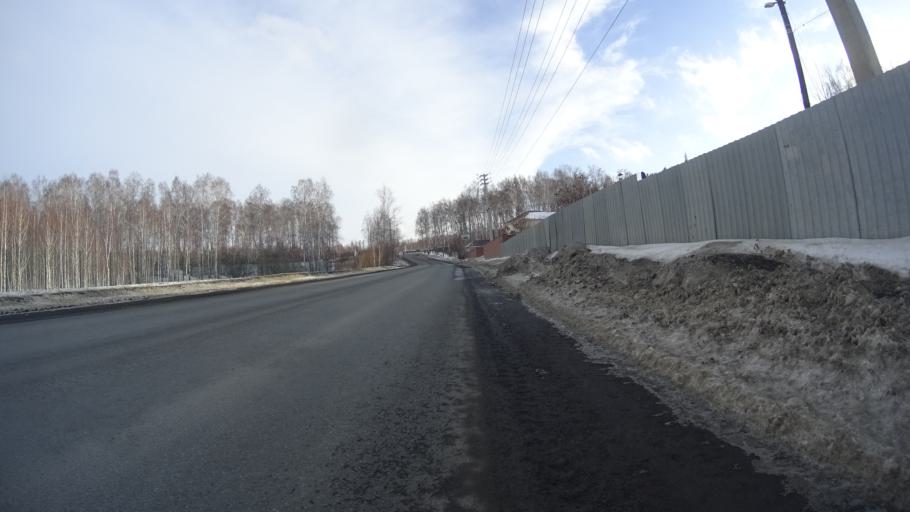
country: RU
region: Chelyabinsk
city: Sargazy
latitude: 55.1299
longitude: 61.2878
